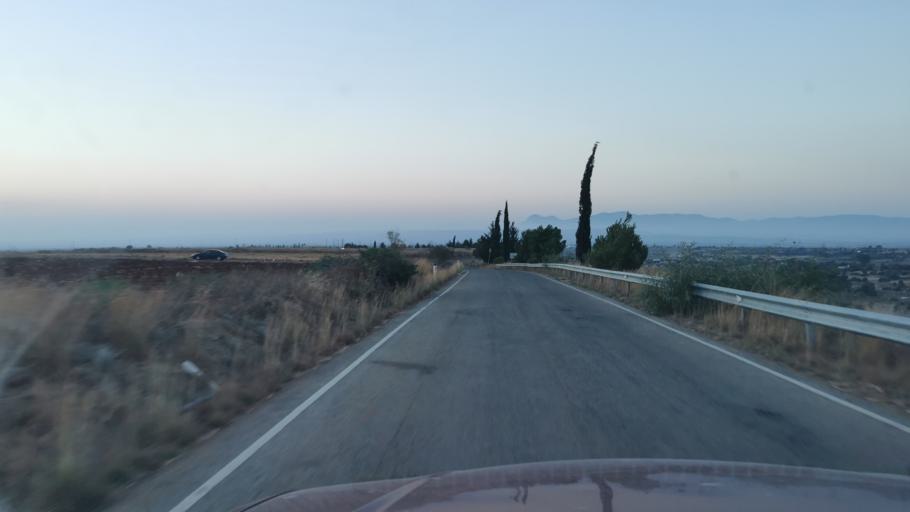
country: CY
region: Lefkosia
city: Peristerona
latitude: 35.0974
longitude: 33.0830
